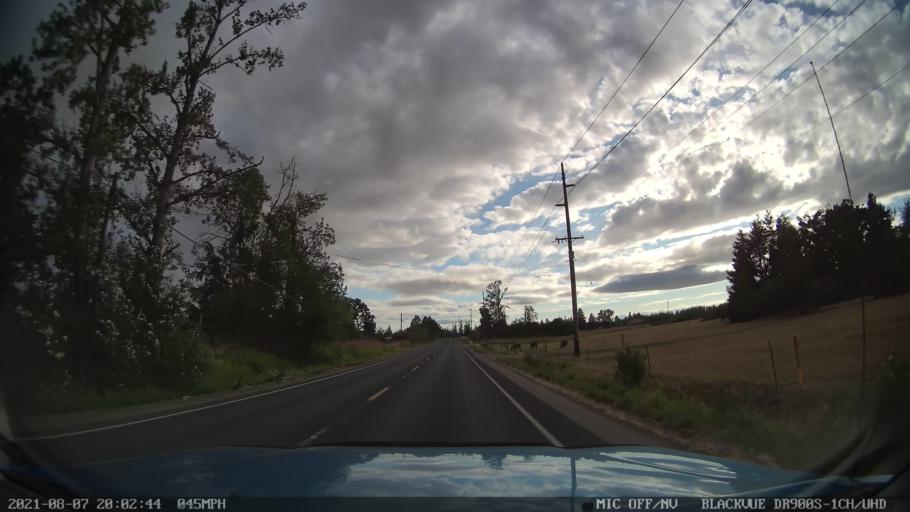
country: US
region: Oregon
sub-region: Marion County
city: Silverton
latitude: 45.0012
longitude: -122.8077
